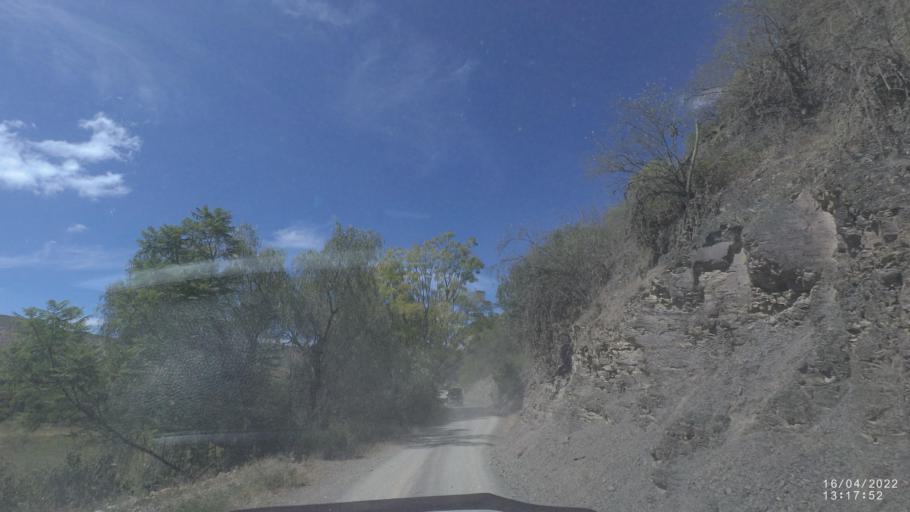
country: BO
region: Cochabamba
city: Mizque
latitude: -17.9877
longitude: -65.6204
